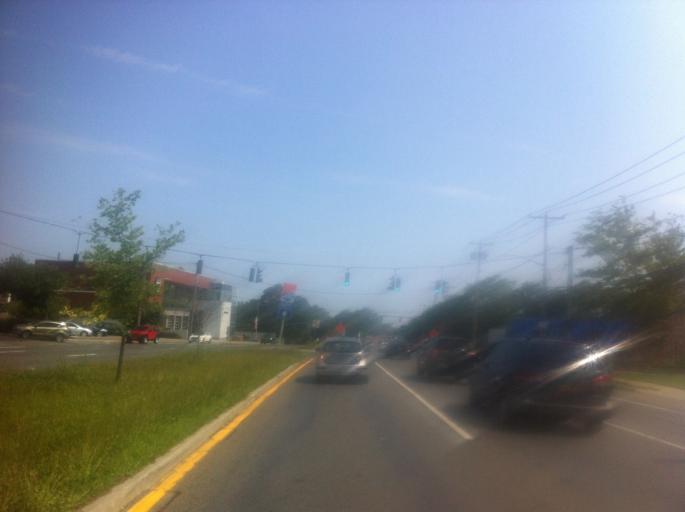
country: US
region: New York
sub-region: Nassau County
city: Jericho
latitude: 40.7888
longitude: -73.5361
